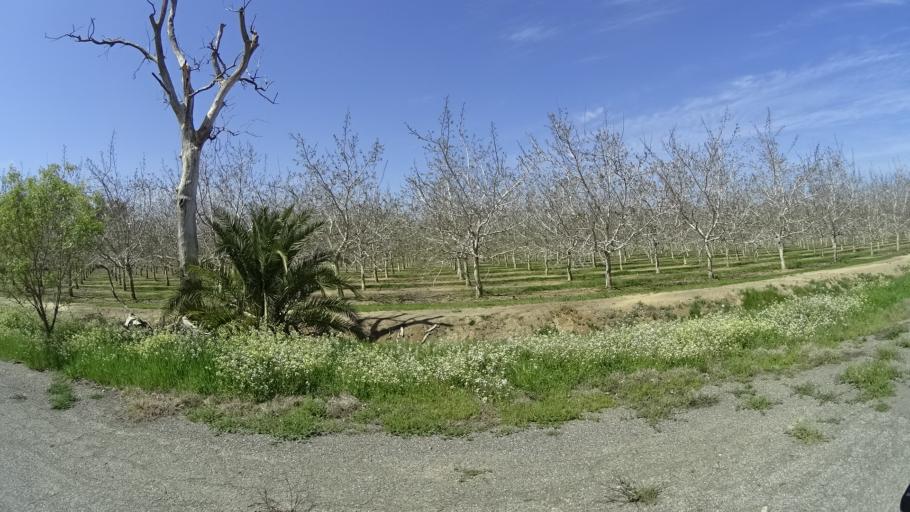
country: US
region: California
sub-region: Glenn County
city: Hamilton City
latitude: 39.6355
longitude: -122.0743
